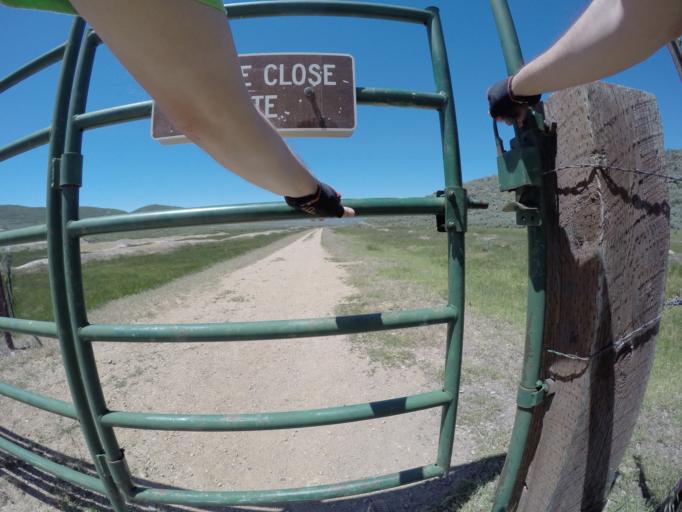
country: US
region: Utah
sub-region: Summit County
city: Park City
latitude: 40.6901
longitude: -111.4584
